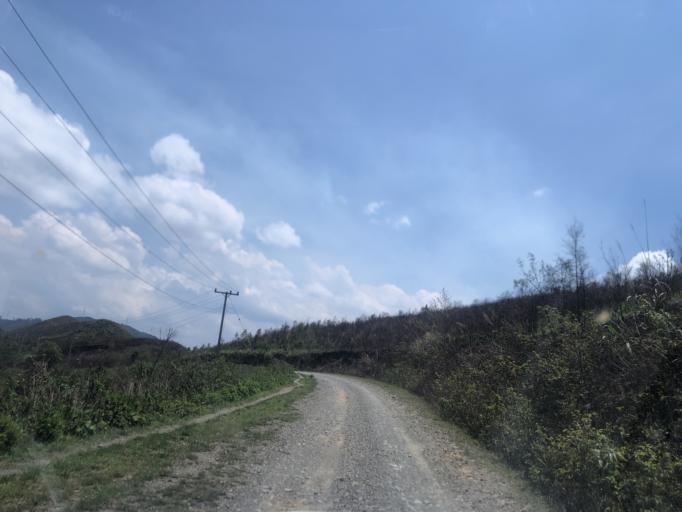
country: LA
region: Phongsali
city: Phongsali
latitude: 21.4190
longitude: 102.1845
